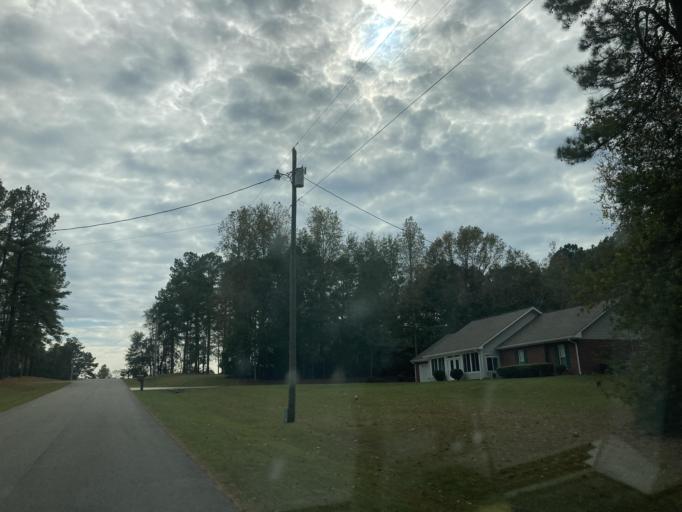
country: US
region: Mississippi
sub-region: Lamar County
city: West Hattiesburg
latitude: 31.2756
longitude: -89.4451
